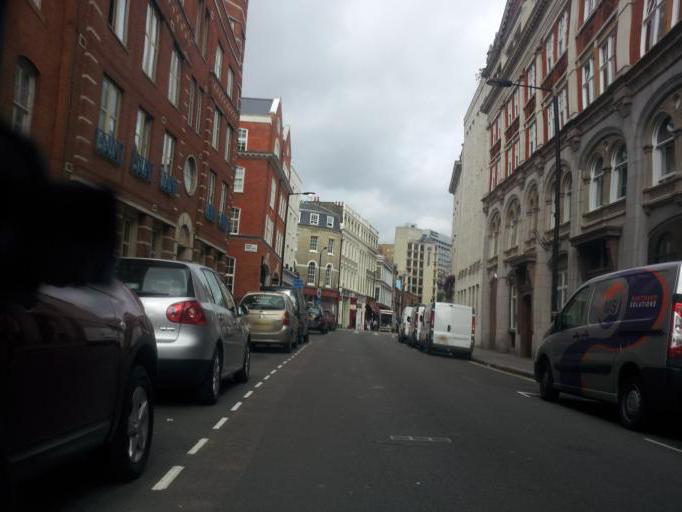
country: GB
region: England
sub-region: Greater London
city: London
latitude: 51.5140
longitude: -0.1211
